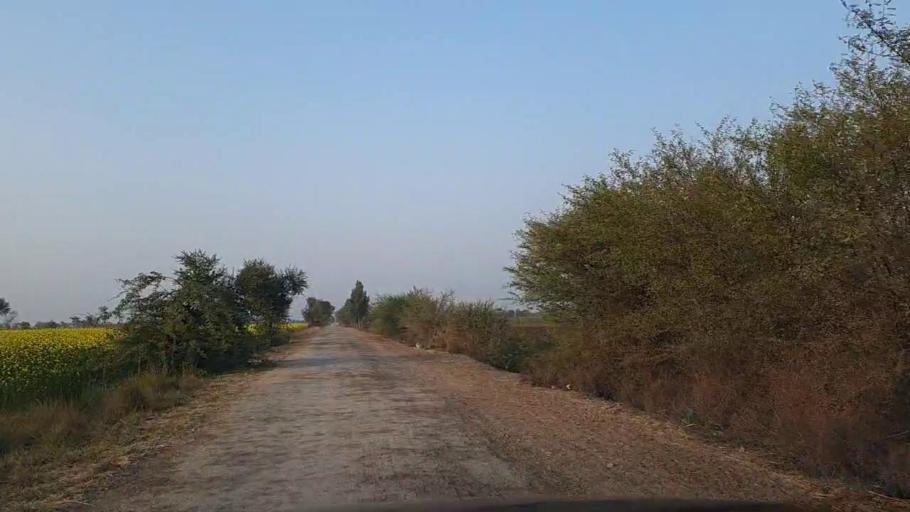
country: PK
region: Sindh
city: Daur
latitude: 26.4220
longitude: 68.3858
